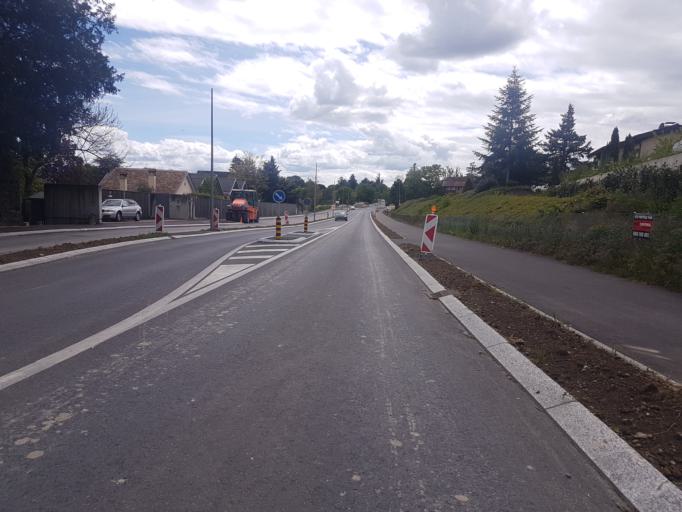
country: CH
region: Vaud
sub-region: Nyon District
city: Coppet
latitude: 46.3069
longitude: 6.1821
